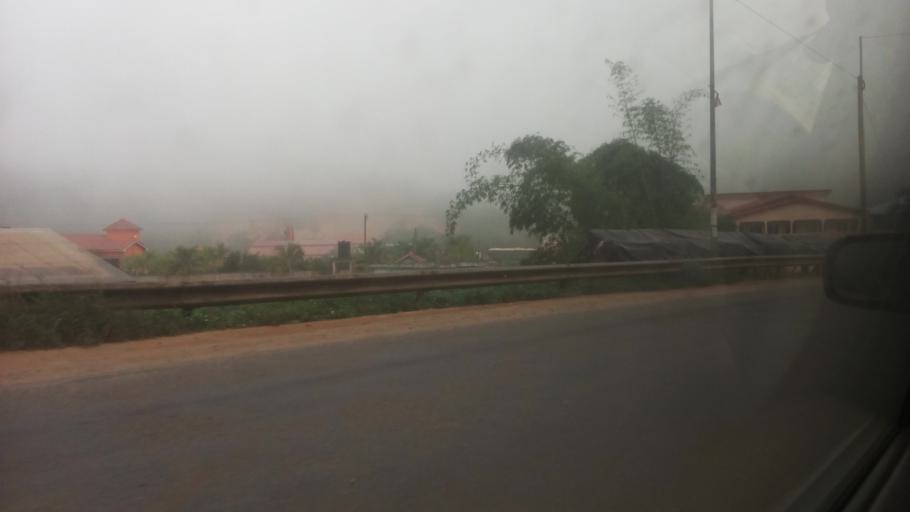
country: GH
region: Western
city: Tarkwa
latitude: 5.2834
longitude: -2.0048
